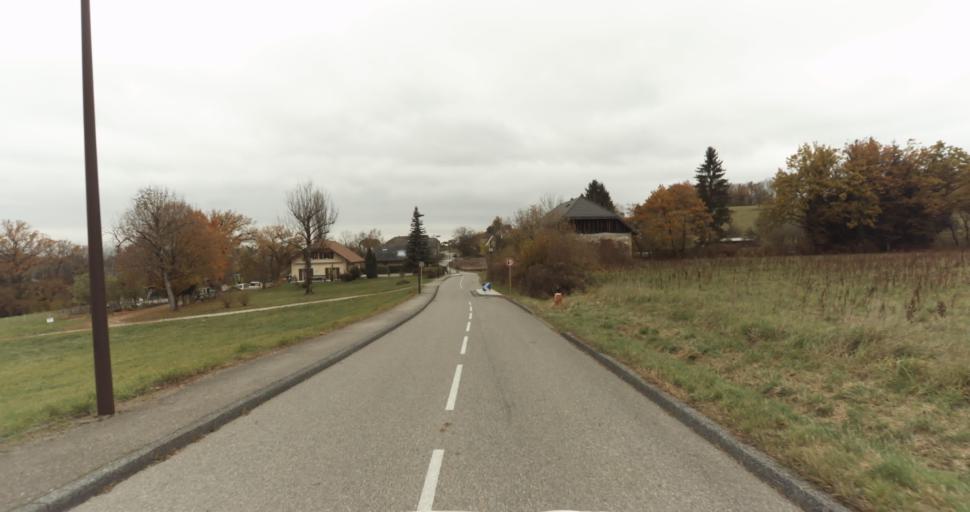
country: FR
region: Rhone-Alpes
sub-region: Departement de la Haute-Savoie
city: Chavanod
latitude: 45.8759
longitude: 6.0627
